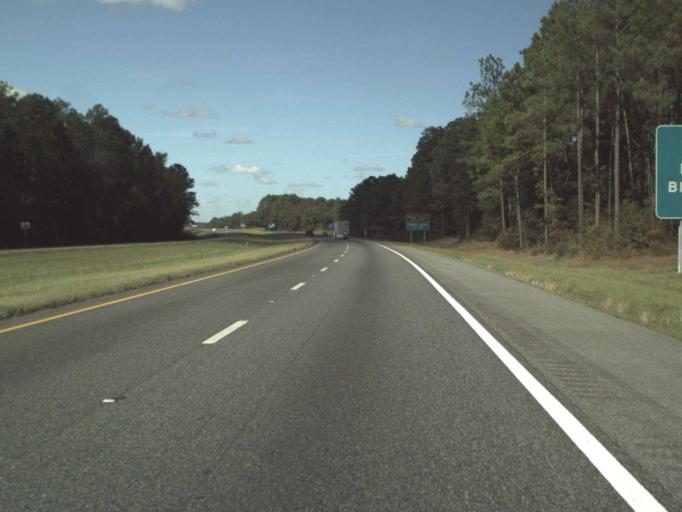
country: US
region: Florida
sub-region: Jackson County
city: Marianna
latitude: 30.7162
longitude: -85.1632
